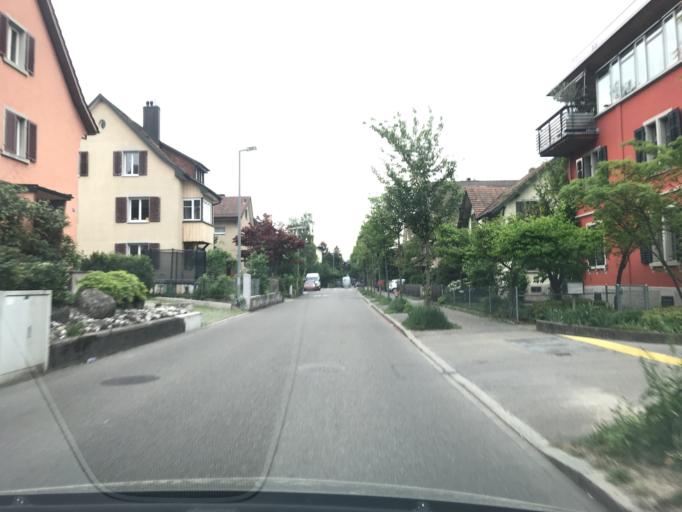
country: CH
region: Zurich
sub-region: Bezirk Winterthur
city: Wuelflingen (Kreis 6) / Oberfeld
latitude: 47.5068
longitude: 8.7030
